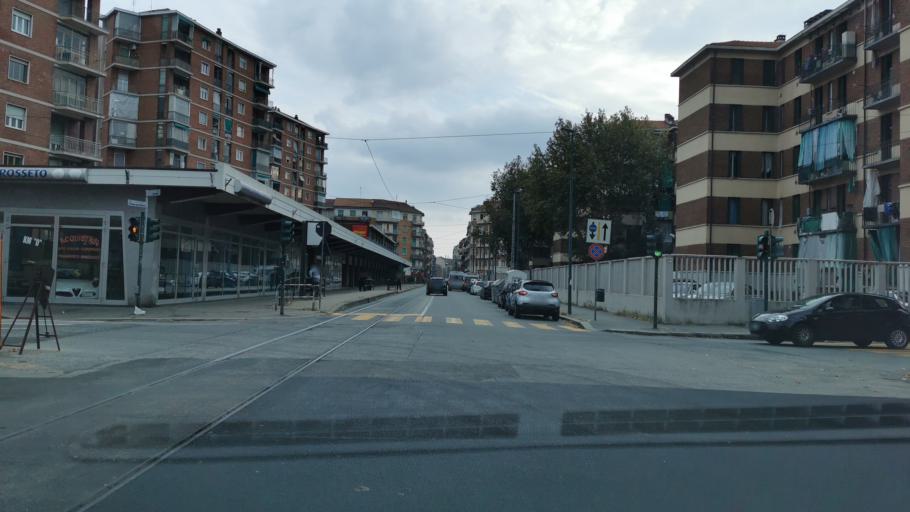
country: IT
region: Piedmont
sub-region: Provincia di Torino
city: Turin
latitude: 45.1043
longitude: 7.6813
